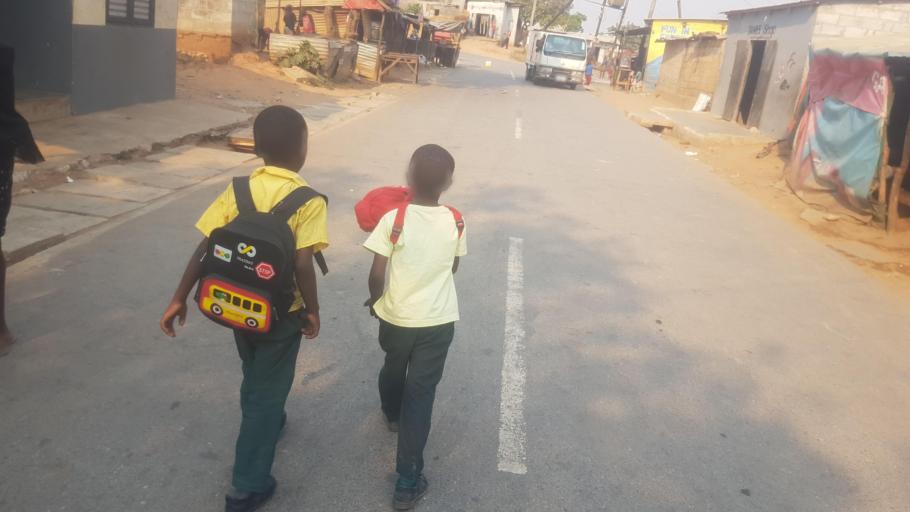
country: ZM
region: Lusaka
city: Lusaka
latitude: -15.4409
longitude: 28.3832
